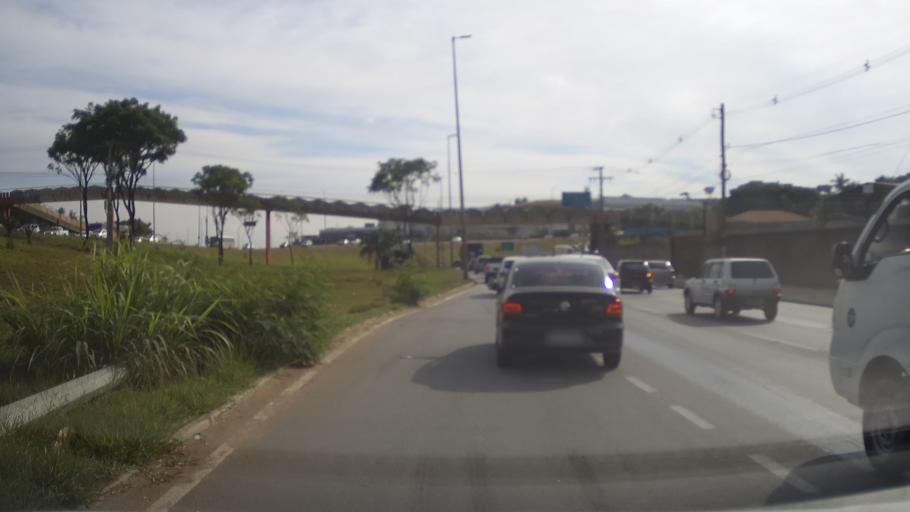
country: BR
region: Minas Gerais
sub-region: Contagem
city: Contagem
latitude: -19.9187
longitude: -44.0568
